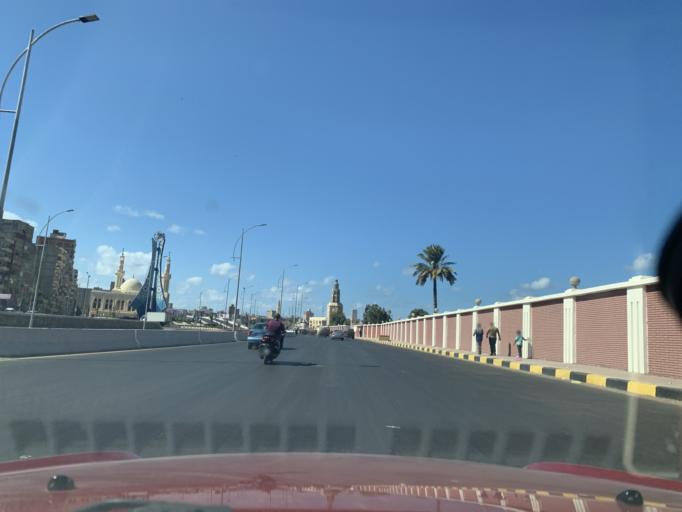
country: EG
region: Alexandria
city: Alexandria
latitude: 31.2213
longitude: 29.9896
